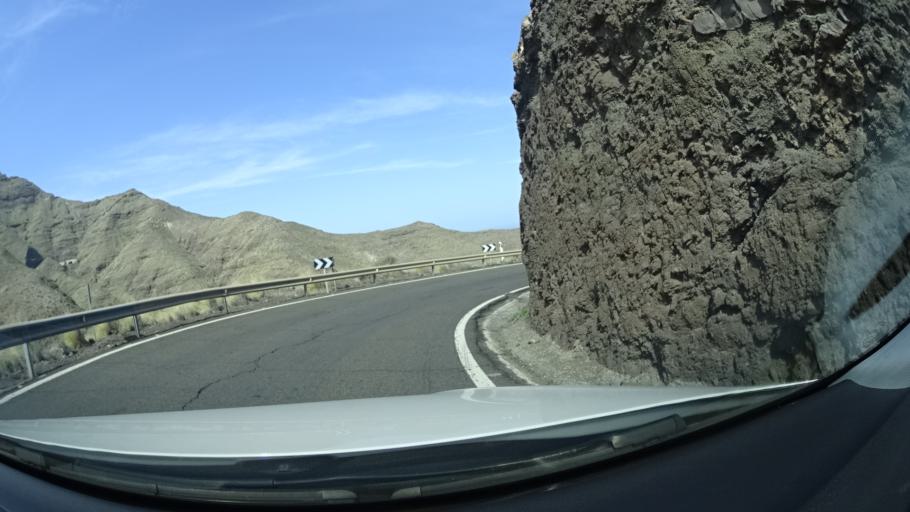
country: ES
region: Canary Islands
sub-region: Provincia de Las Palmas
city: Agaete
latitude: 28.0424
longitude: -15.7351
